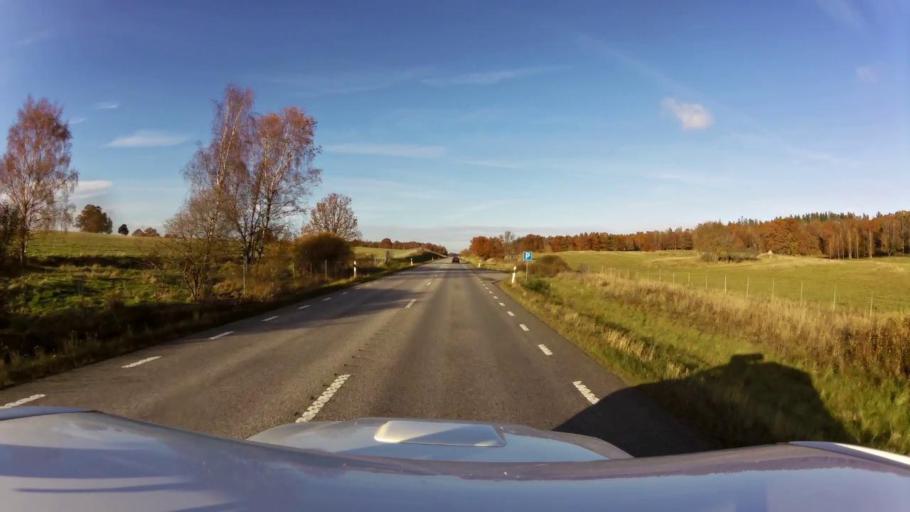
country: SE
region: OEstergoetland
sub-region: Kinda Kommun
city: Rimforsa
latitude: 58.1984
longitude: 15.6676
